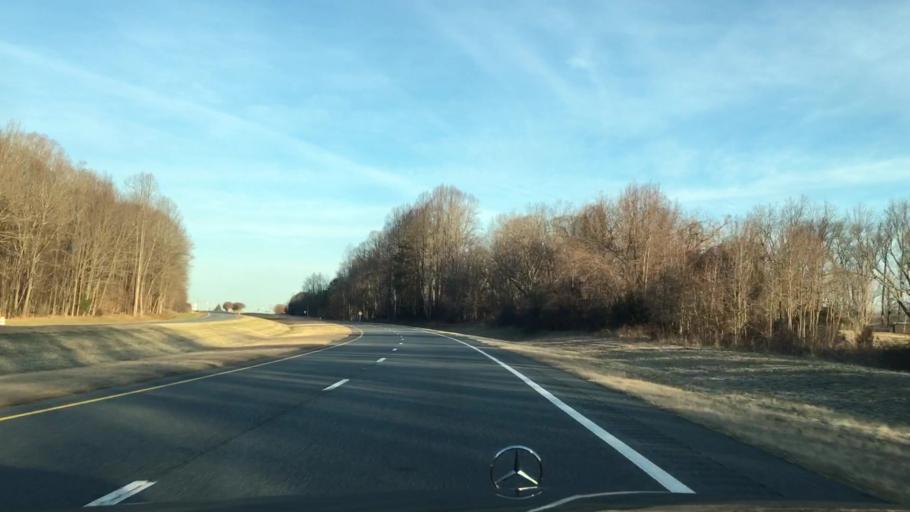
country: US
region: North Carolina
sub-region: Guilford County
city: Greensboro
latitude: 36.0231
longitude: -79.7646
